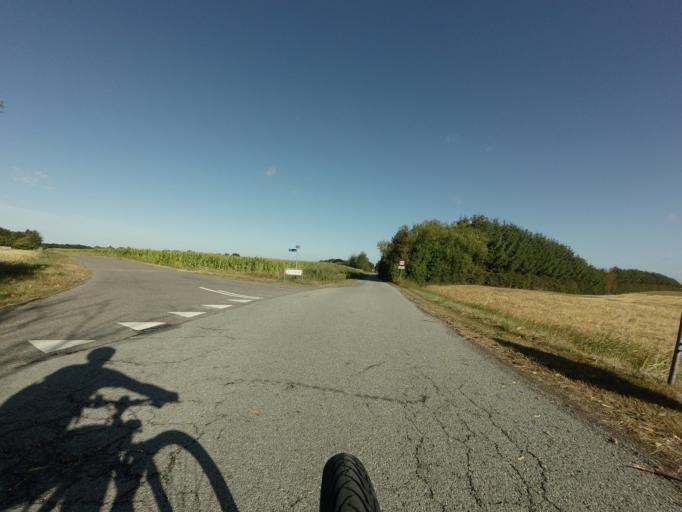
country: DK
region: North Denmark
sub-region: Hjorring Kommune
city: Vra
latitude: 57.3838
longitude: 9.9627
